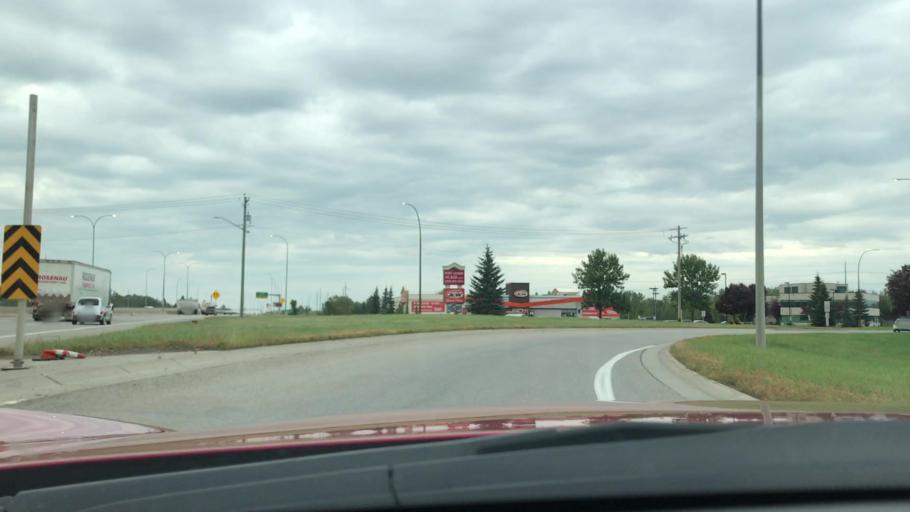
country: CA
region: Alberta
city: Calgary
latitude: 50.9896
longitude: -114.0290
